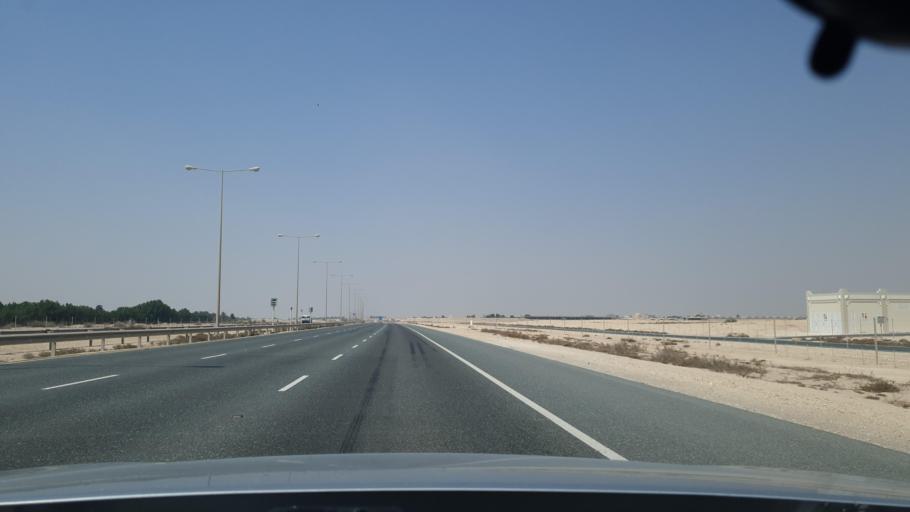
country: QA
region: Al Khawr
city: Al Khawr
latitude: 25.7753
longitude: 51.4094
